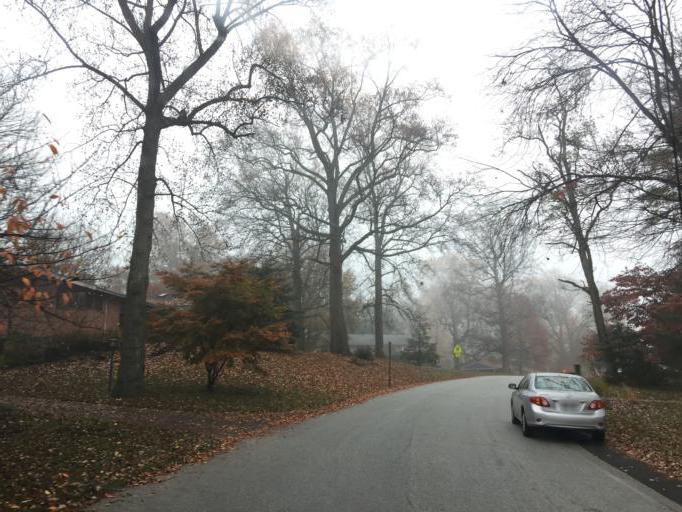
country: US
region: Maryland
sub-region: Howard County
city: Riverside
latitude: 39.1872
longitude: -76.8580
